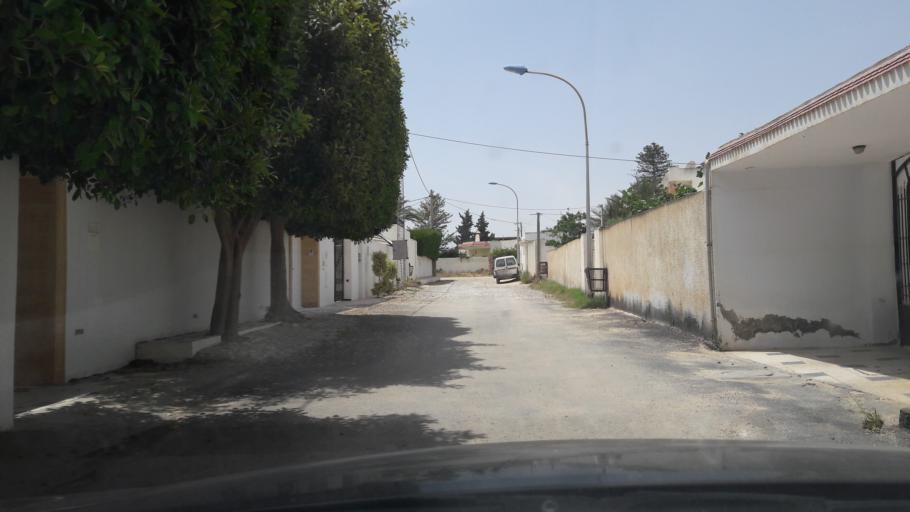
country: TN
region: Safaqis
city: Al Qarmadah
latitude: 34.7827
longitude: 10.7581
